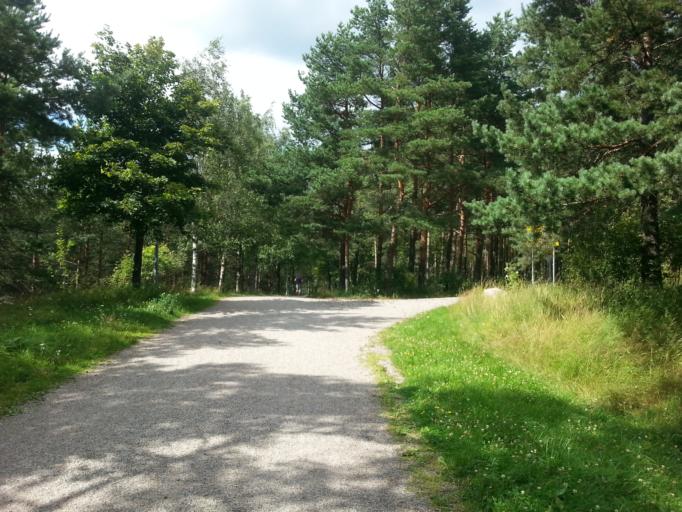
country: FI
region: Paijanne Tavastia
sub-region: Lahti
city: Lahti
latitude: 60.9786
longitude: 25.6450
